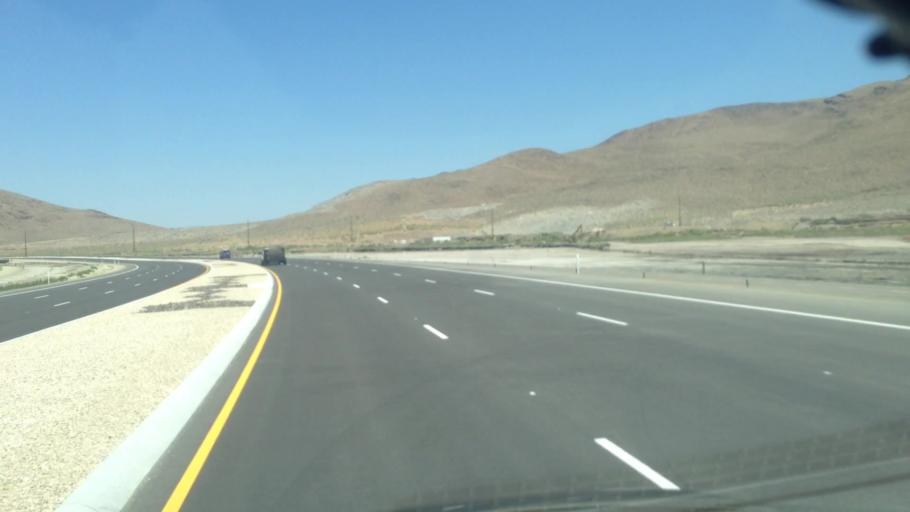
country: US
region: Nevada
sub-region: Washoe County
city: Sparks
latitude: 39.4551
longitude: -119.7251
